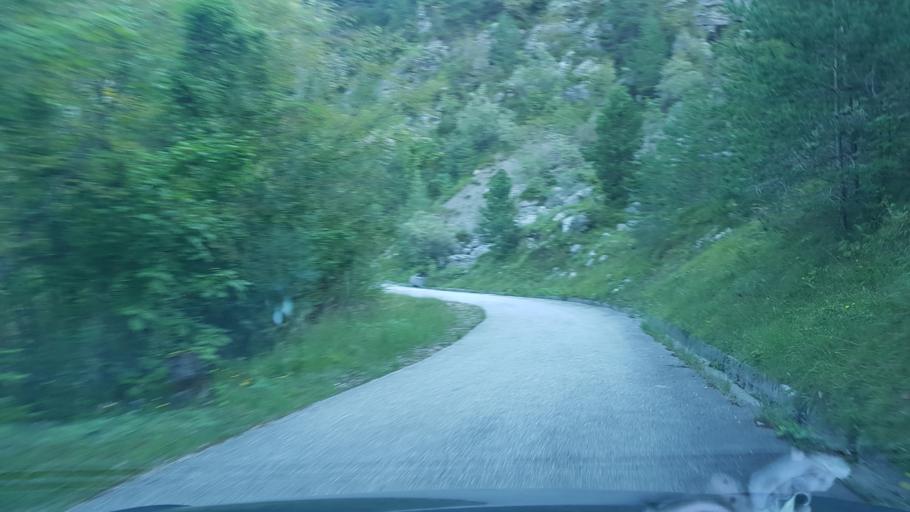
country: IT
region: Friuli Venezia Giulia
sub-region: Provincia di Pordenone
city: Frisanco
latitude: 46.2596
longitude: 12.7032
